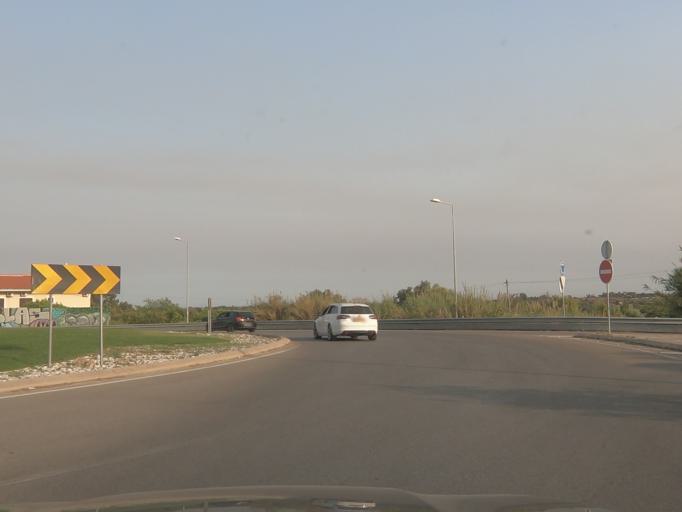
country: PT
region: Faro
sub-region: Loule
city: Almancil
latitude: 37.0934
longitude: -8.0607
